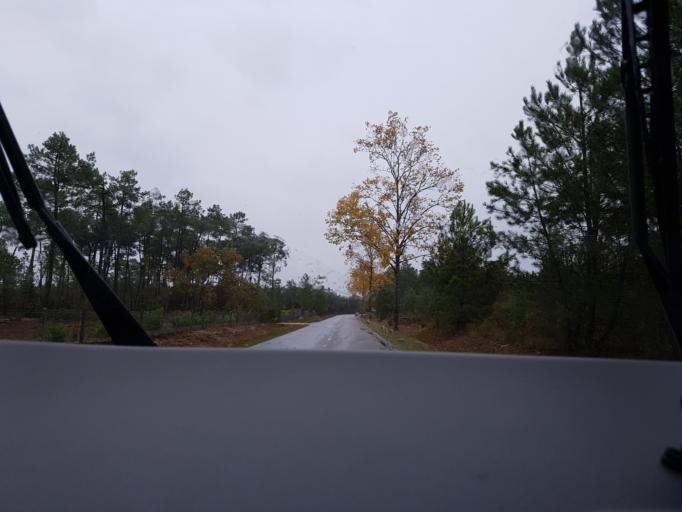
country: FR
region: Aquitaine
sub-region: Departement de la Gironde
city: Saint-Symphorien
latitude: 44.3108
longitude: -0.5891
